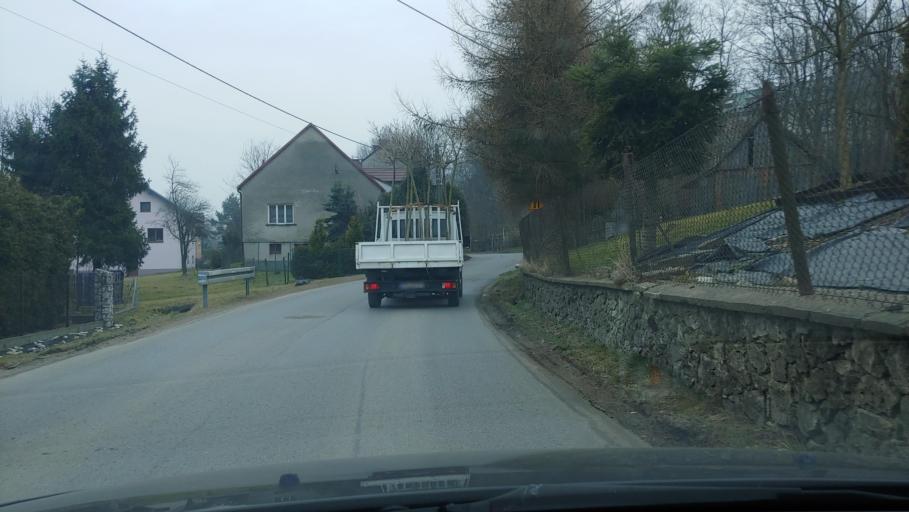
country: PL
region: Lesser Poland Voivodeship
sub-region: Powiat krakowski
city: Balice
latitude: 50.0891
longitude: 19.7883
